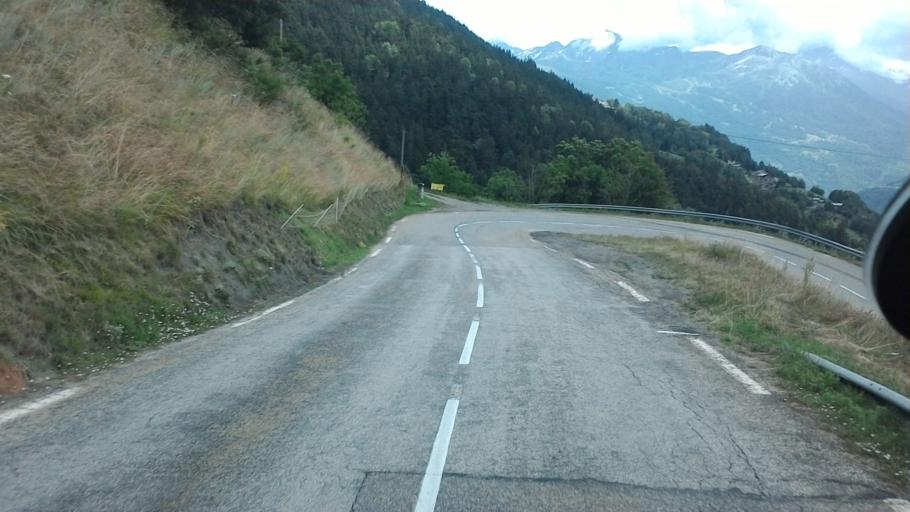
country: FR
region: Rhone-Alpes
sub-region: Departement de la Savoie
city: Seez
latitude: 45.6232
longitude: 6.8277
